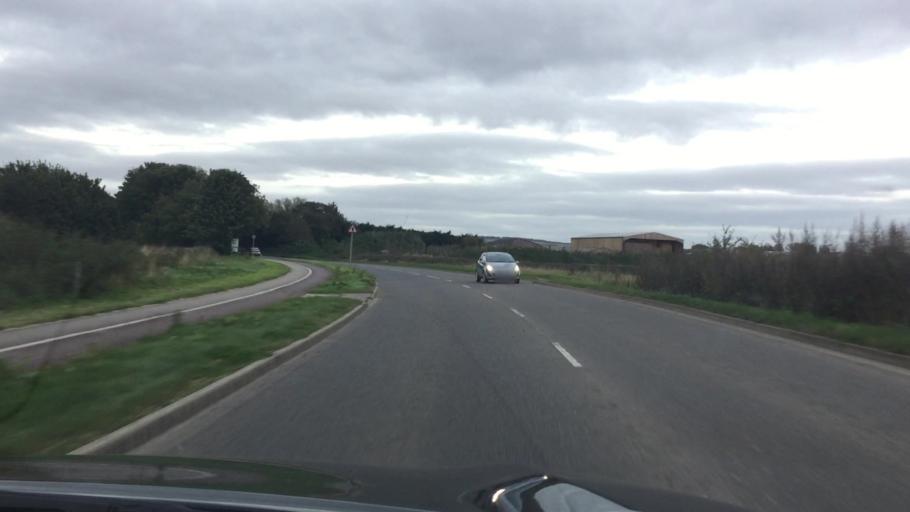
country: GB
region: England
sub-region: East Riding of Yorkshire
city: Pocklington
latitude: 53.9212
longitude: -0.7930
